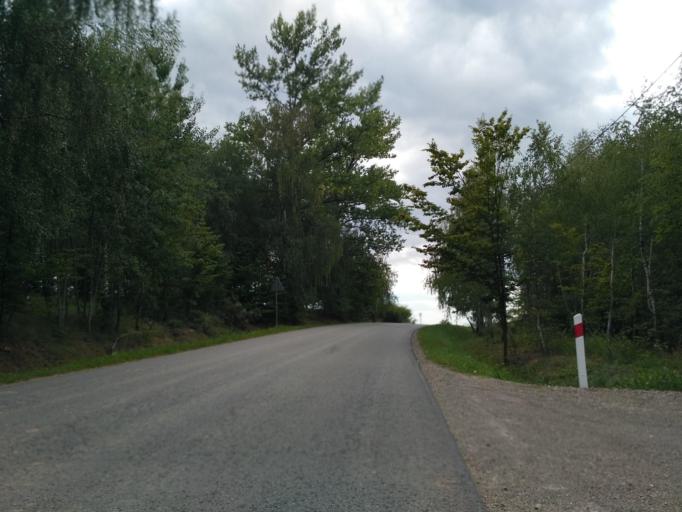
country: PL
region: Subcarpathian Voivodeship
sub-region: Powiat rzeszowski
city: Straszydle
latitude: 49.8829
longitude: 21.9910
